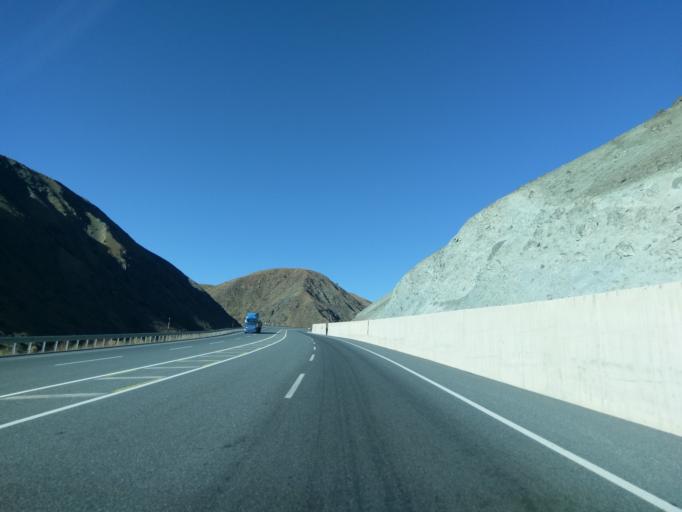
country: TR
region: Erzincan
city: Catalarmut
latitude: 39.8846
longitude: 39.1828
